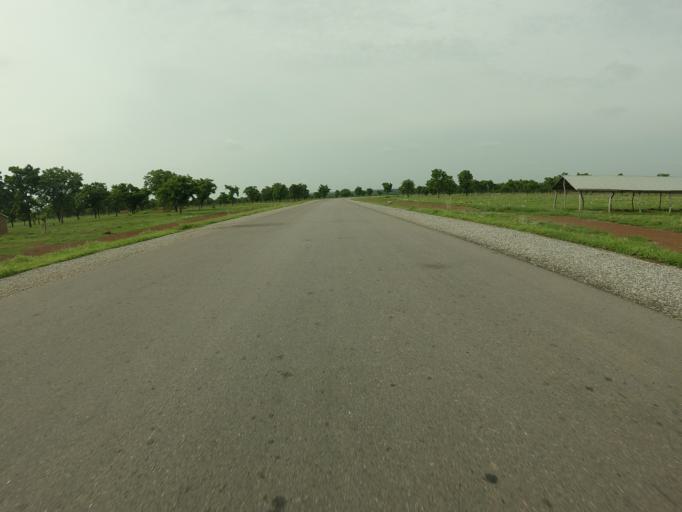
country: GH
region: Northern
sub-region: Yendi
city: Yendi
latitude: 9.8080
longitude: -0.1140
